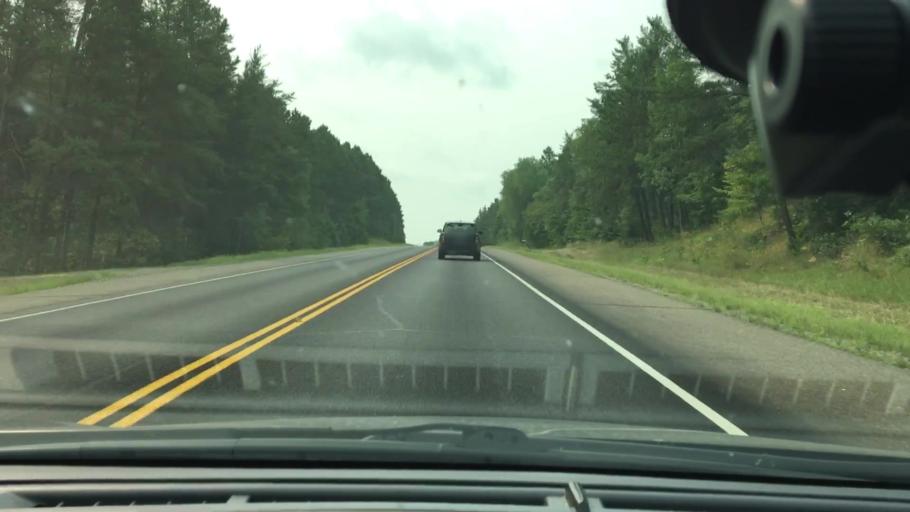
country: US
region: Minnesota
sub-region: Crow Wing County
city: Cross Lake
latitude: 46.6250
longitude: -94.1317
